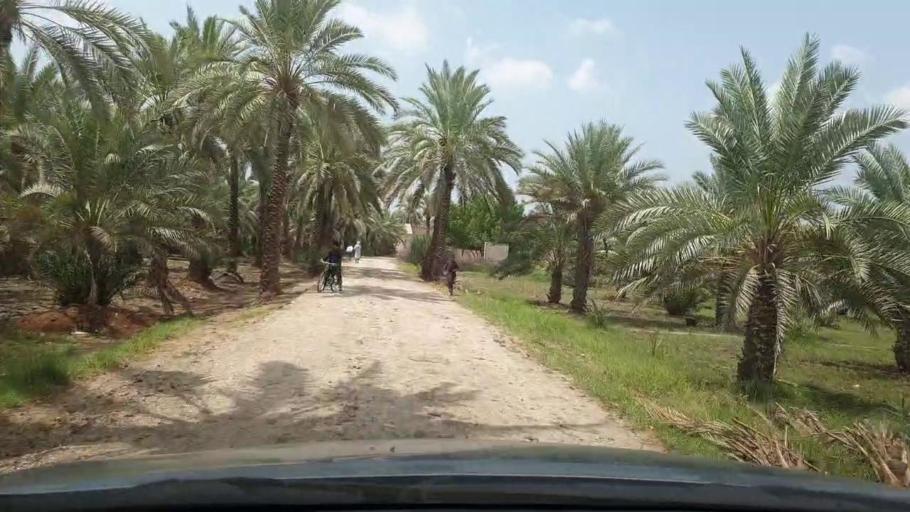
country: PK
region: Sindh
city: Kot Diji
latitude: 27.4042
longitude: 68.7566
